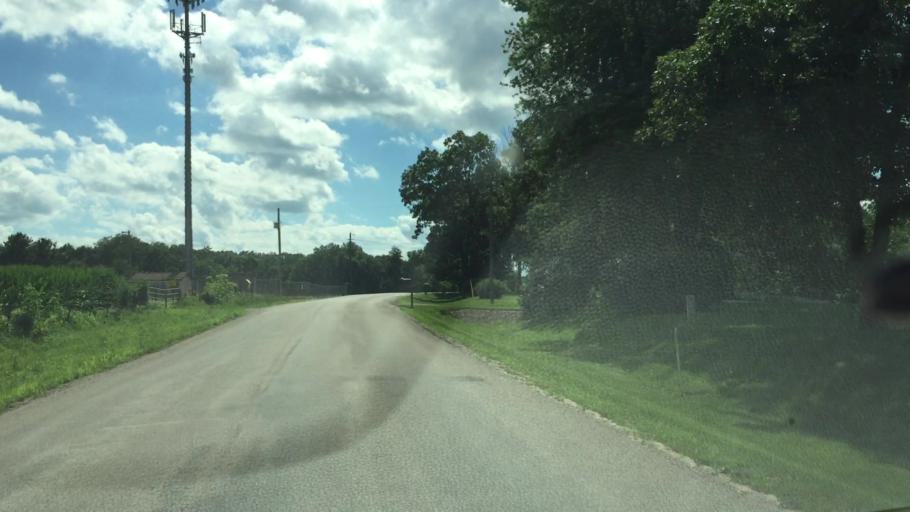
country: US
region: Iowa
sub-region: Linn County
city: Ely
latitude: 41.8277
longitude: -91.6214
